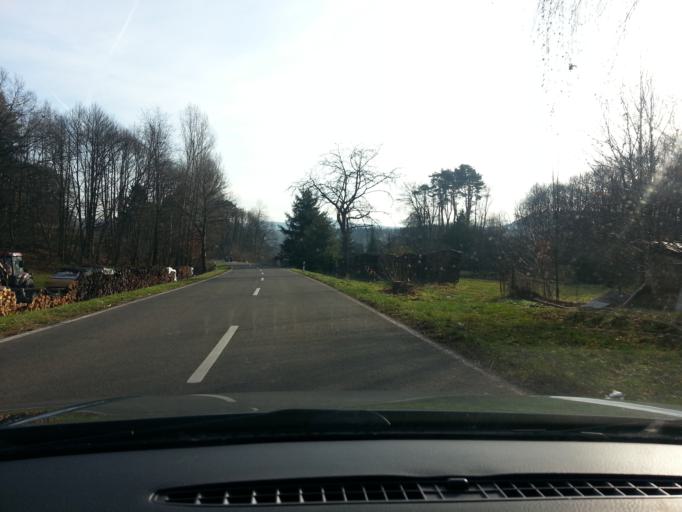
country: DE
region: Rheinland-Pfalz
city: Volkersweiler
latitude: 49.1737
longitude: 7.9277
